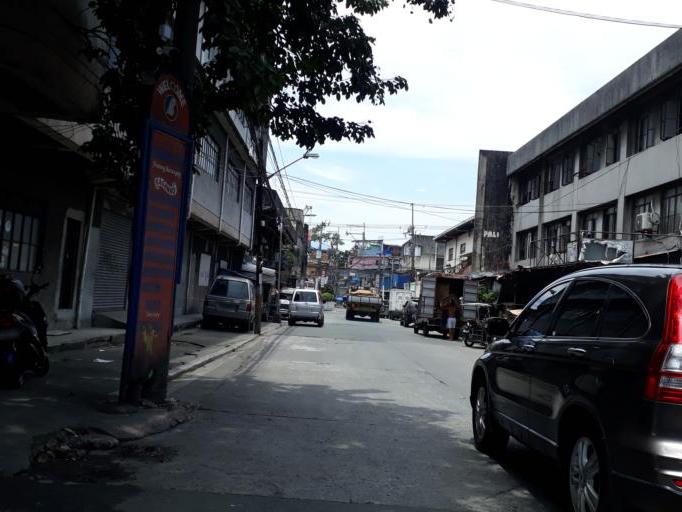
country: PH
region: Metro Manila
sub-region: Caloocan City
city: Niugan
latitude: 14.6460
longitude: 120.9786
